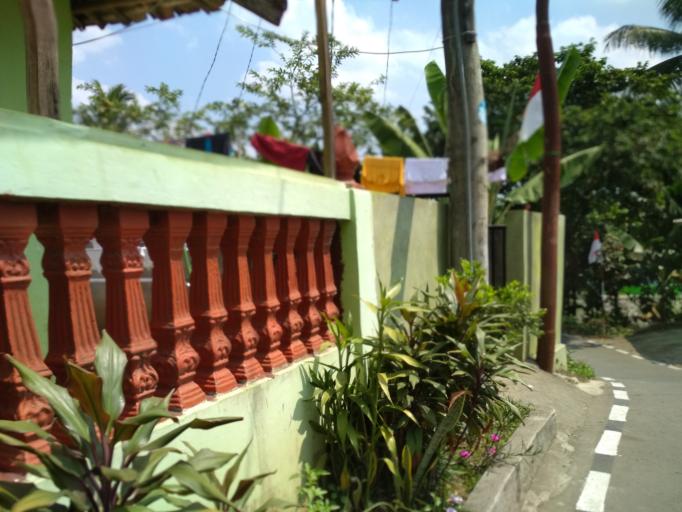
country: ID
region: West Java
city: Ciampea
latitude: -6.5636
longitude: 106.7479
